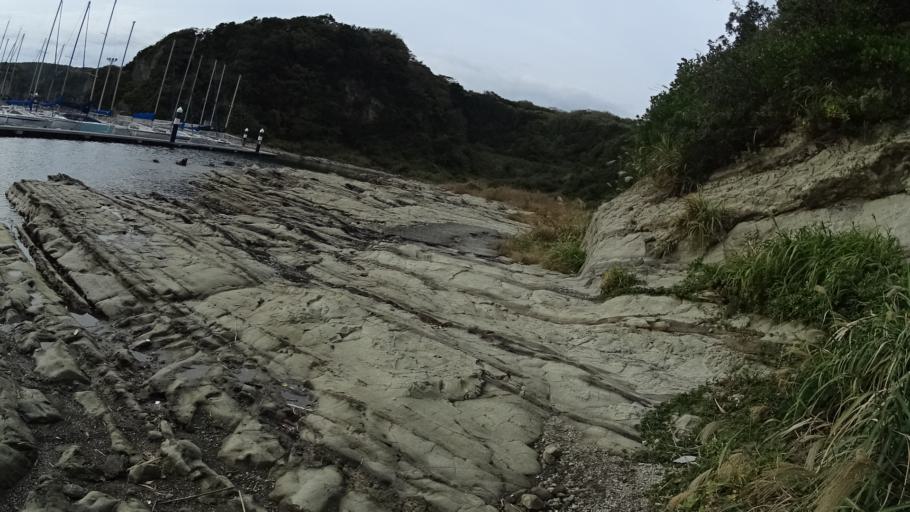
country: JP
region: Kanagawa
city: Miura
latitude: 35.1406
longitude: 139.6406
